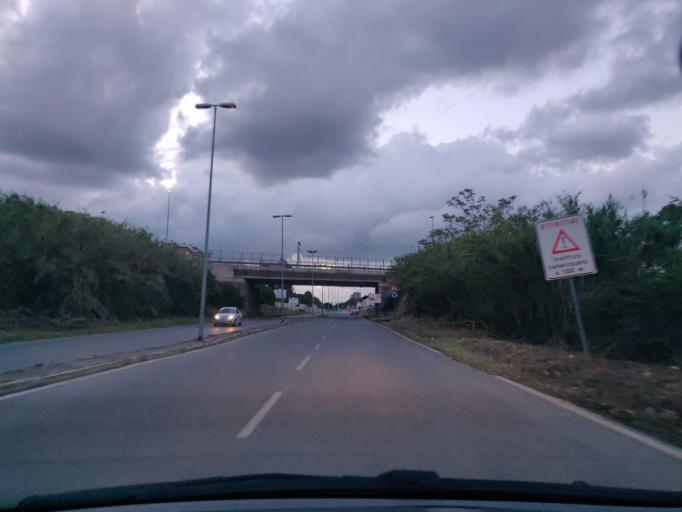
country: IT
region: Latium
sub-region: Citta metropolitana di Roma Capitale
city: Civitavecchia
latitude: 42.1038
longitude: 11.7919
